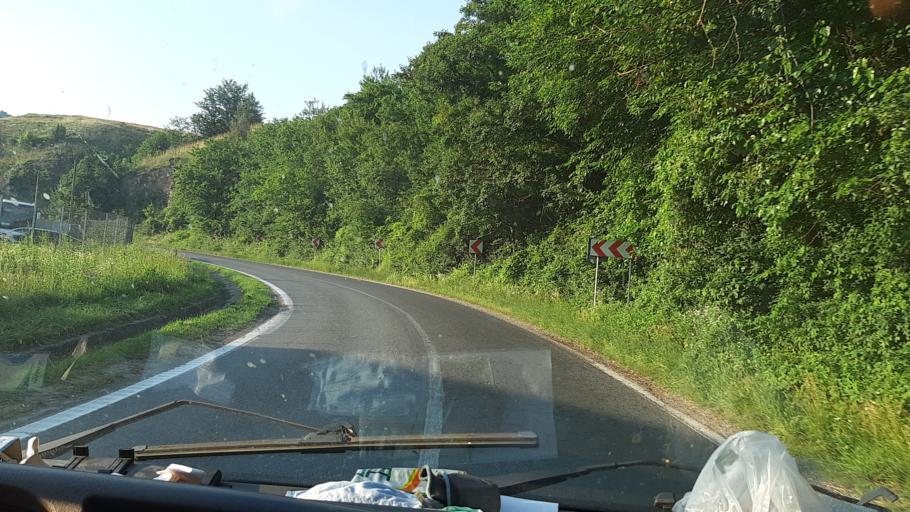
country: RO
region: Caras-Severin
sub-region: Municipiul Resita
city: Calnic
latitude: 45.3489
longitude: 21.8370
